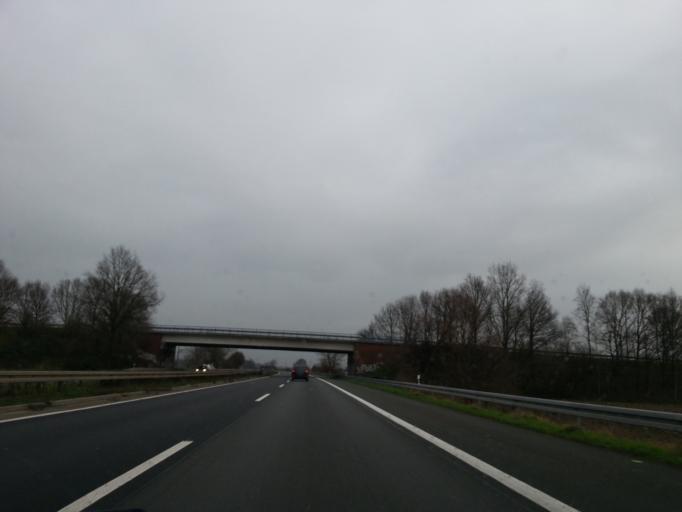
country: NL
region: Gelderland
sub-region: Gemeente Montferland
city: s-Heerenberg
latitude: 51.8506
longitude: 6.2933
